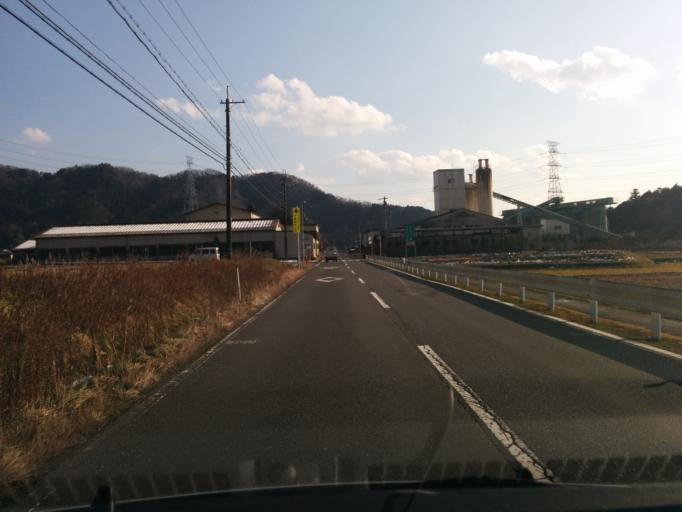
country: JP
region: Kyoto
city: Ayabe
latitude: 35.3520
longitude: 135.2208
